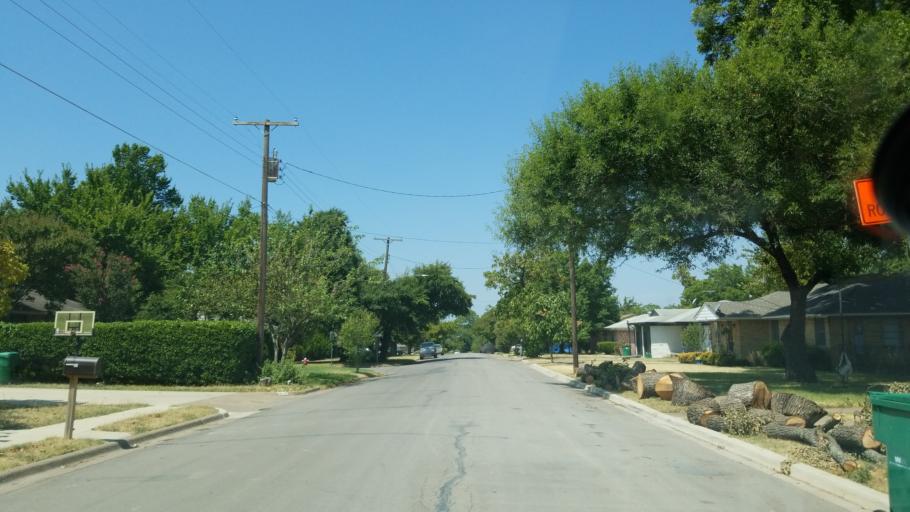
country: US
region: Texas
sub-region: Dallas County
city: Cockrell Hill
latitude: 32.7342
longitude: -96.8923
